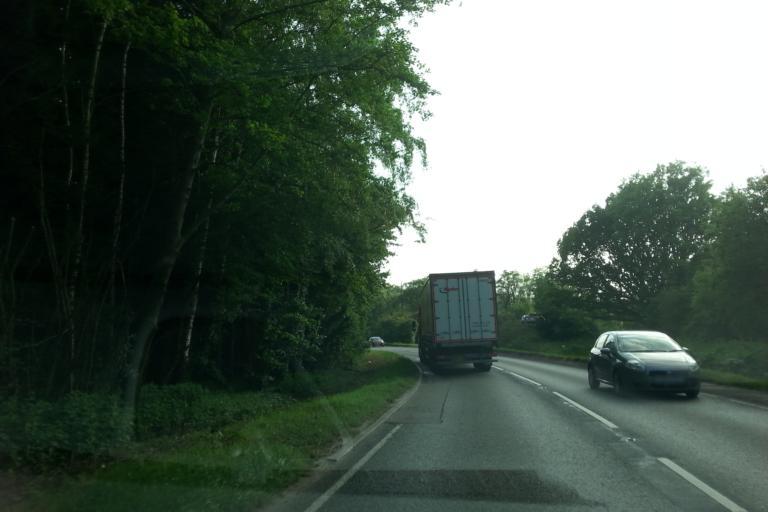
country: GB
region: England
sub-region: Cambridgeshire
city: Hemingford Grey
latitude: 52.3070
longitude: -0.0890
